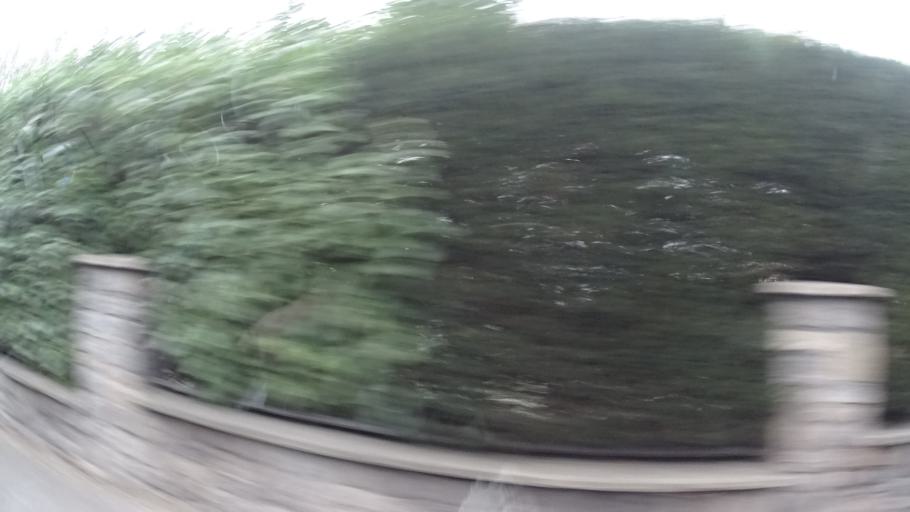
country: DE
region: Bavaria
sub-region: Regierungsbezirk Unterfranken
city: Alzenau in Unterfranken
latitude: 50.0520
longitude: 9.0668
